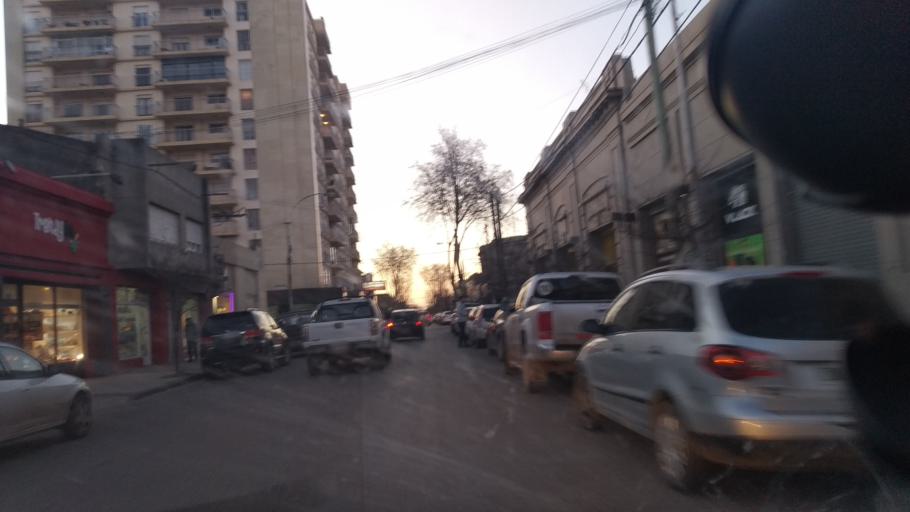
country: AR
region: Buenos Aires
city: Necochea
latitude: -38.5549
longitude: -58.7428
